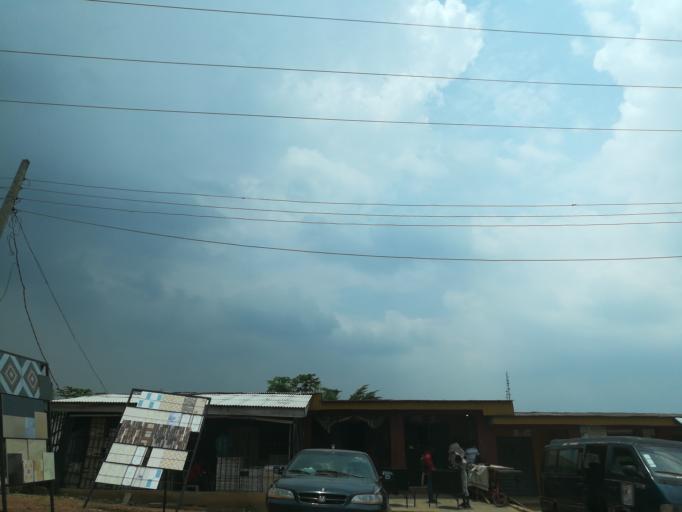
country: NG
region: Lagos
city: Ikorodu
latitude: 6.6055
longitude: 3.5862
